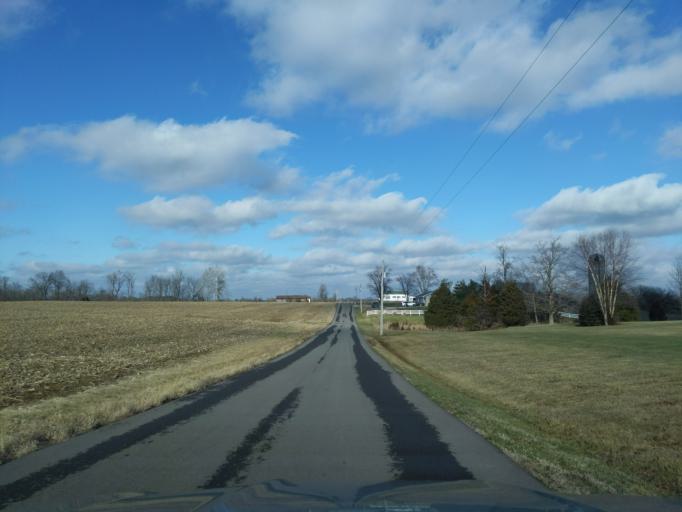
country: US
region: Indiana
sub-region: Decatur County
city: Greensburg
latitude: 39.2655
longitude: -85.4839
